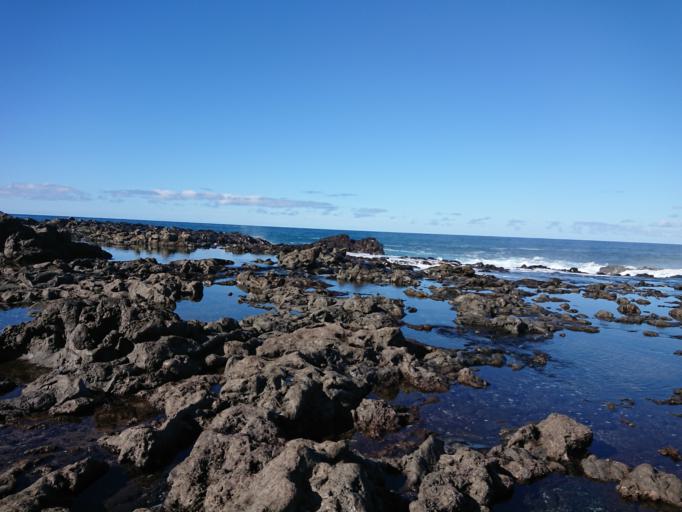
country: ES
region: Canary Islands
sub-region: Provincia de Las Palmas
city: Tinajo
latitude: 29.0834
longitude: -13.7253
